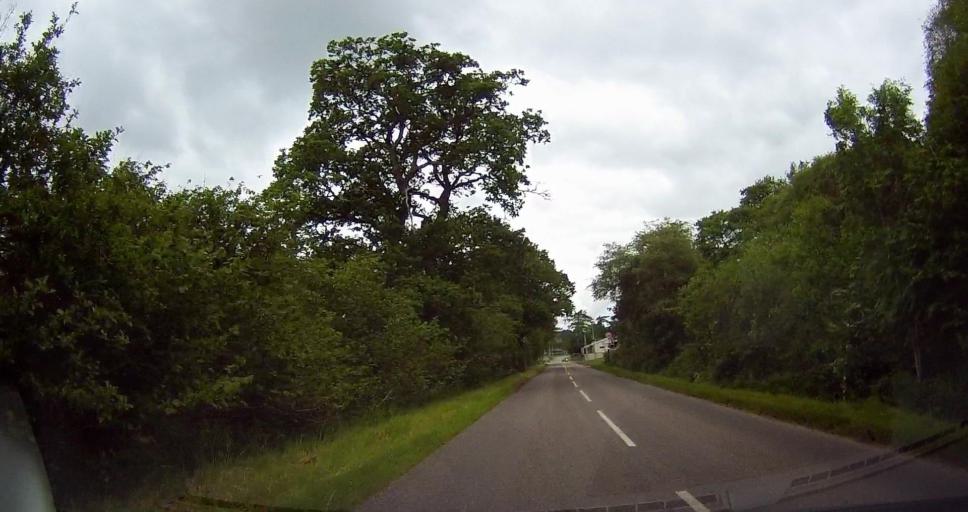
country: GB
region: Scotland
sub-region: Highland
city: Dornoch
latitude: 57.9856
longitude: -4.1510
